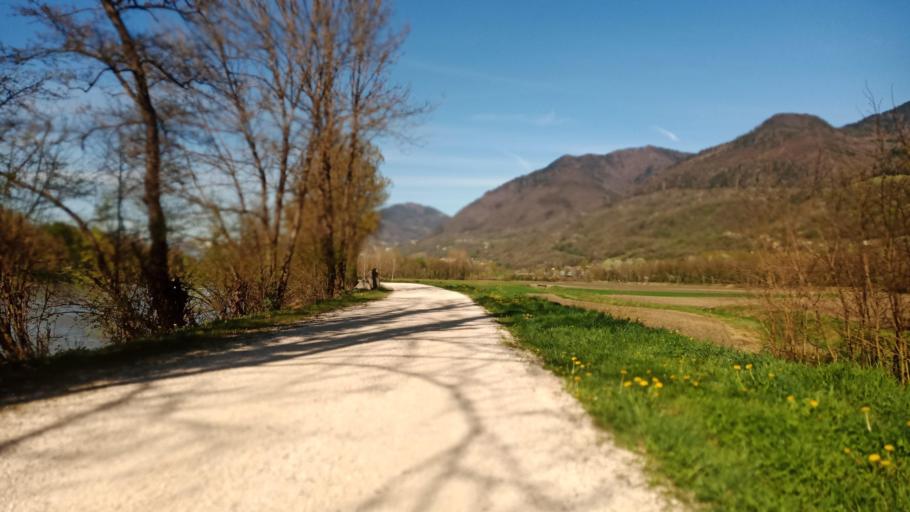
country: FR
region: Rhone-Alpes
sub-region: Departement de l'Isere
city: Tencin
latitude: 45.3222
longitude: 5.9556
